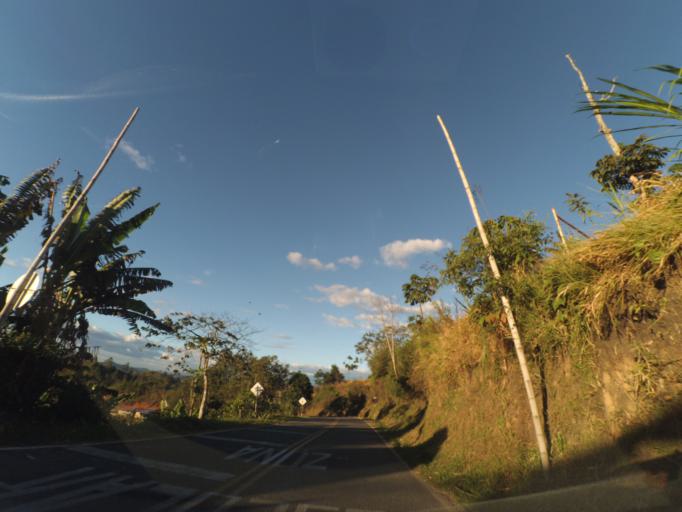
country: CO
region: Cauca
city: Lopez
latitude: 2.4300
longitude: -76.7491
